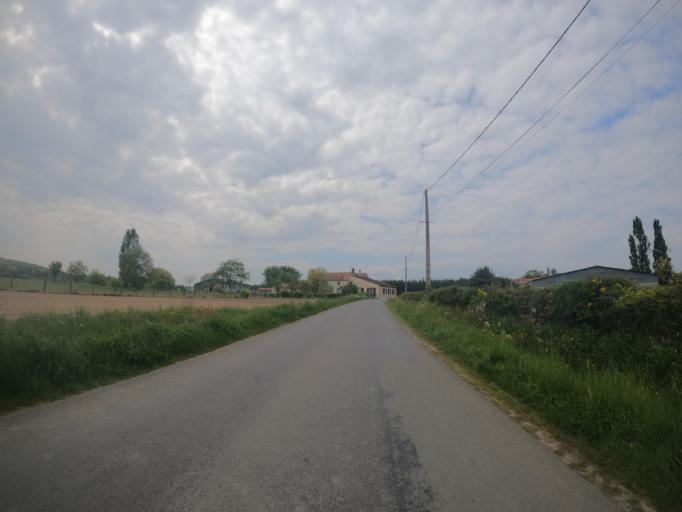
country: FR
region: Poitou-Charentes
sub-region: Departement des Deux-Sevres
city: Saint-Varent
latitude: 46.8627
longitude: -0.2751
